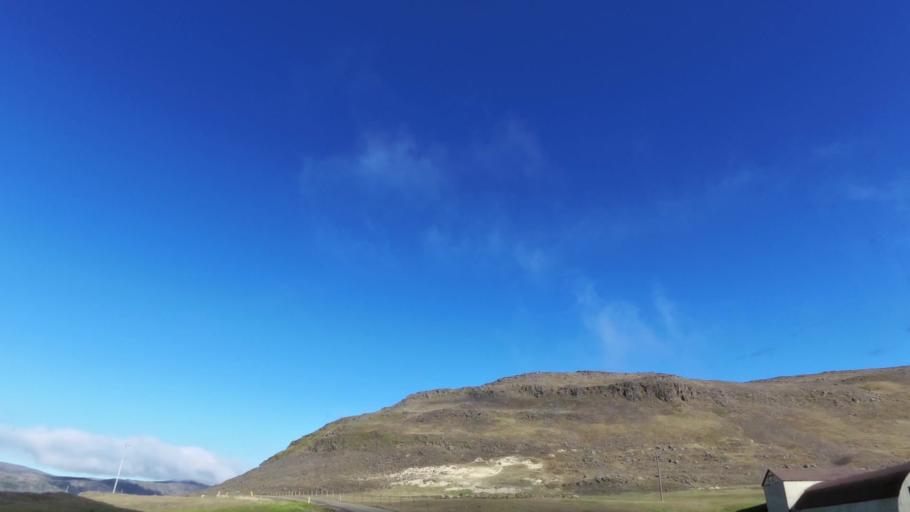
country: IS
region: West
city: Olafsvik
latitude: 65.5591
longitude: -24.0118
